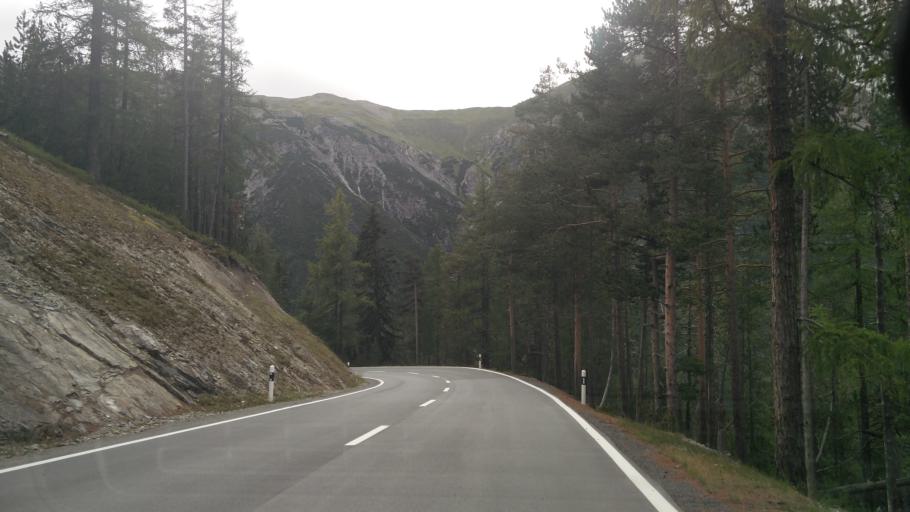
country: CH
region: Grisons
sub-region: Inn District
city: Zernez
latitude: 46.6714
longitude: 10.1670
